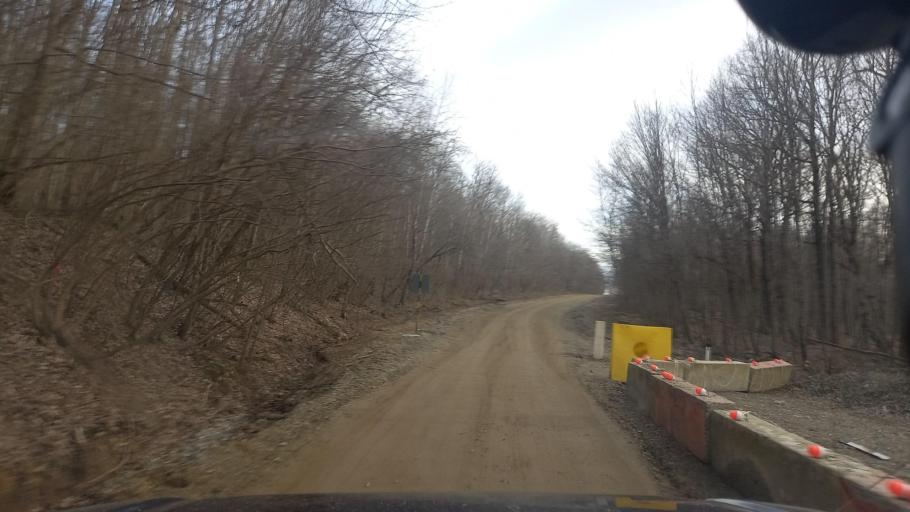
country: RU
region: Krasnodarskiy
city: Goryachiy Klyuch
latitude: 44.7052
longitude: 39.0155
